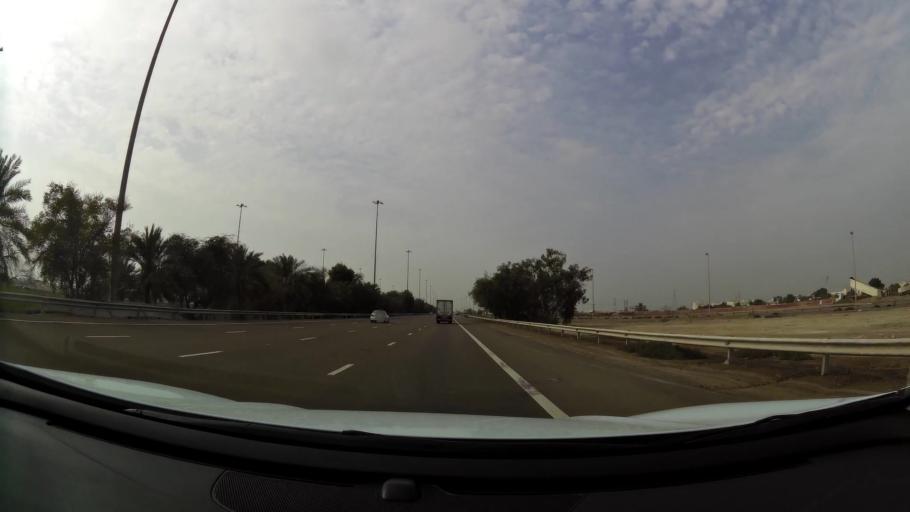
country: AE
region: Abu Dhabi
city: Abu Dhabi
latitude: 24.6688
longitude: 54.7594
